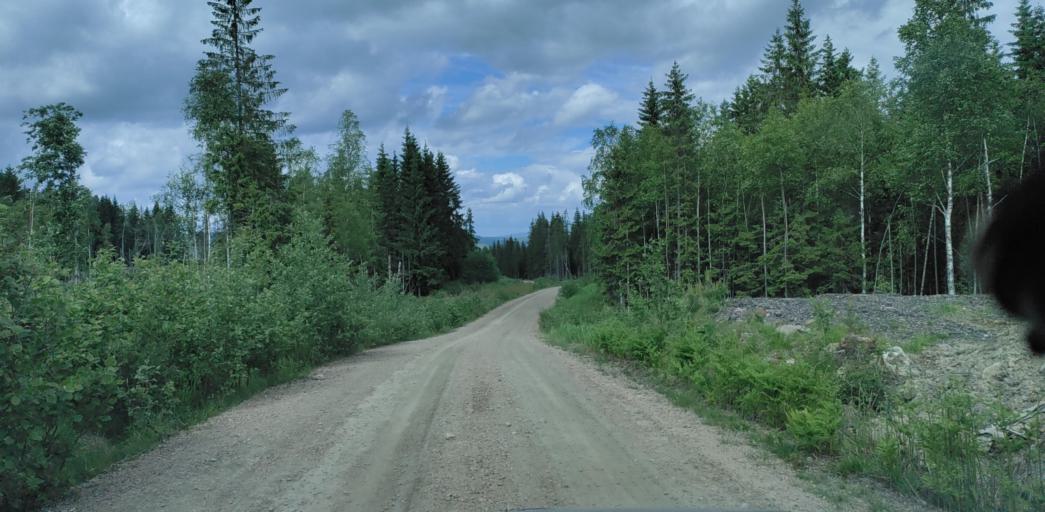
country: SE
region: Vaermland
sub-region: Munkfors Kommun
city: Munkfors
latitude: 59.9563
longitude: 13.4114
